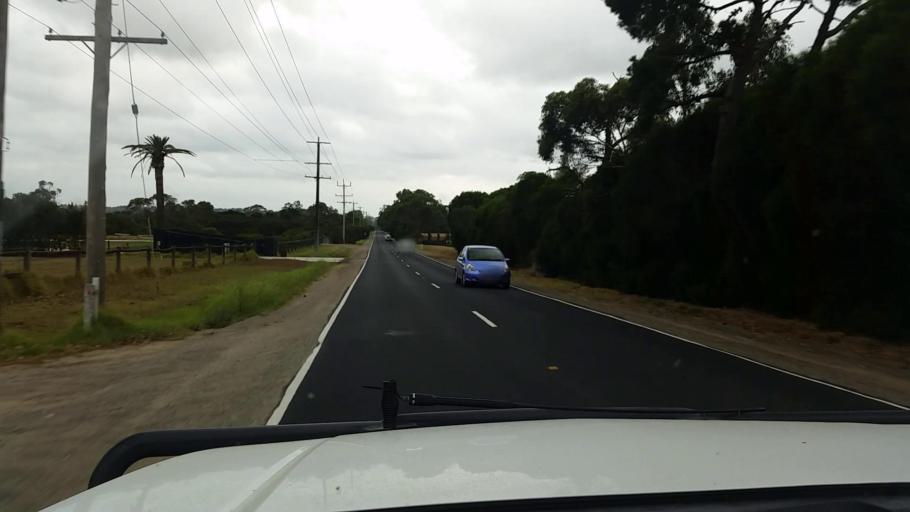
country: AU
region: Victoria
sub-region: Mornington Peninsula
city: Somerville
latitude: -38.2162
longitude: 145.1560
